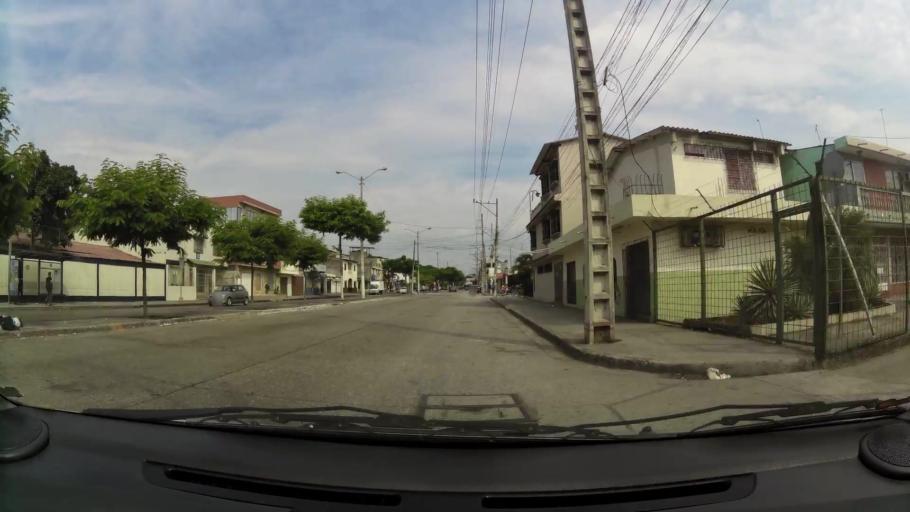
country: EC
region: Guayas
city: Guayaquil
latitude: -2.2477
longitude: -79.8998
